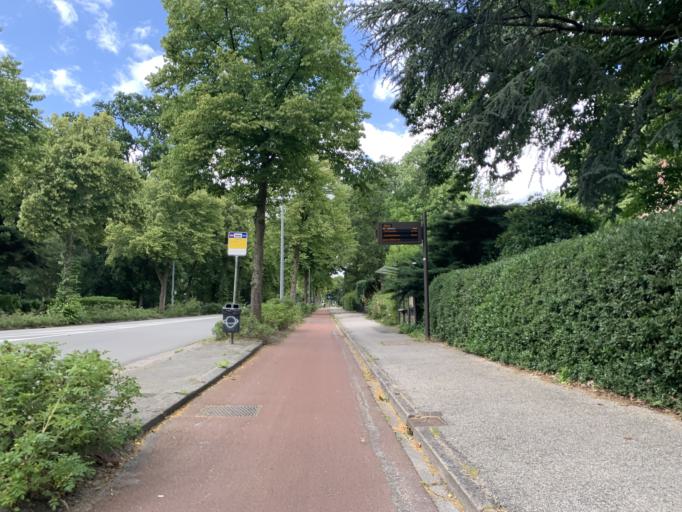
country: NL
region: Groningen
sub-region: Gemeente Haren
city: Haren
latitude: 53.1879
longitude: 6.5861
